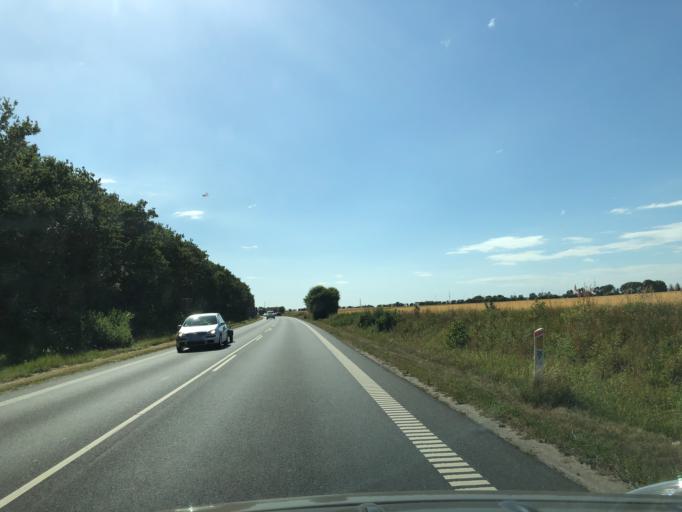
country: DK
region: North Denmark
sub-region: Vesthimmerland Kommune
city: Alestrup
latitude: 56.6213
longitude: 9.5010
